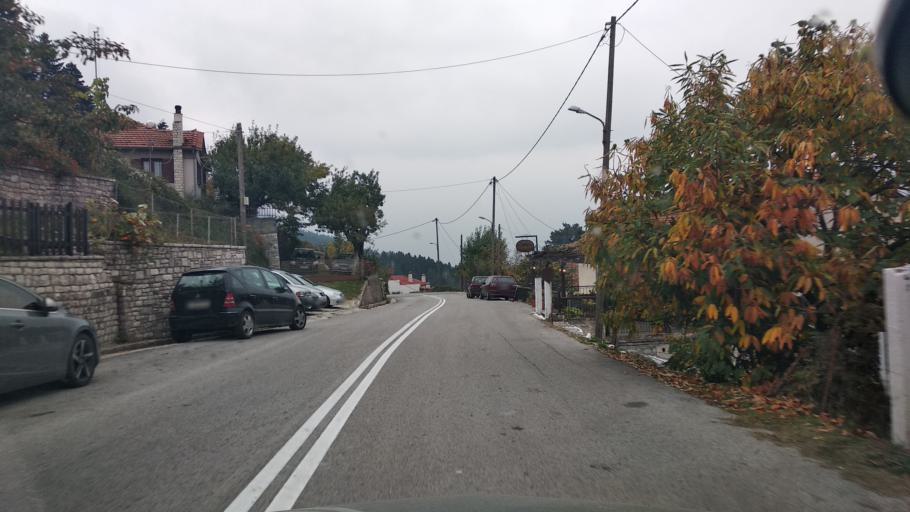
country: GR
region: Thessaly
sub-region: Trikala
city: Pyli
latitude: 39.5050
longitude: 21.5352
